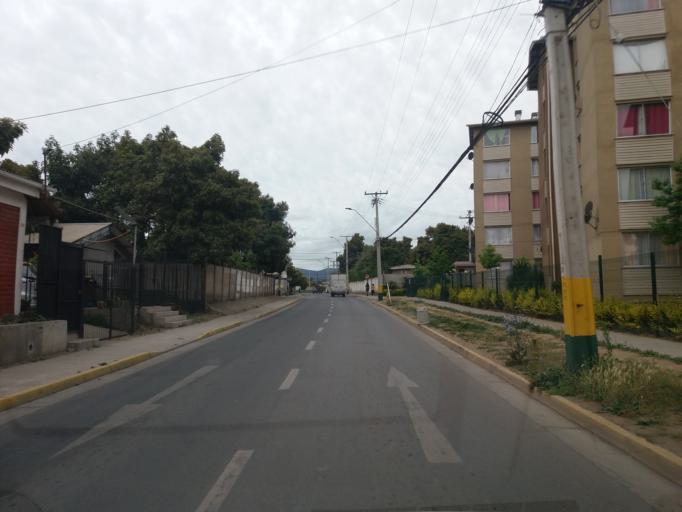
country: CL
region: Valparaiso
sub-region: Provincia de Quillota
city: Quillota
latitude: -32.8435
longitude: -71.2274
